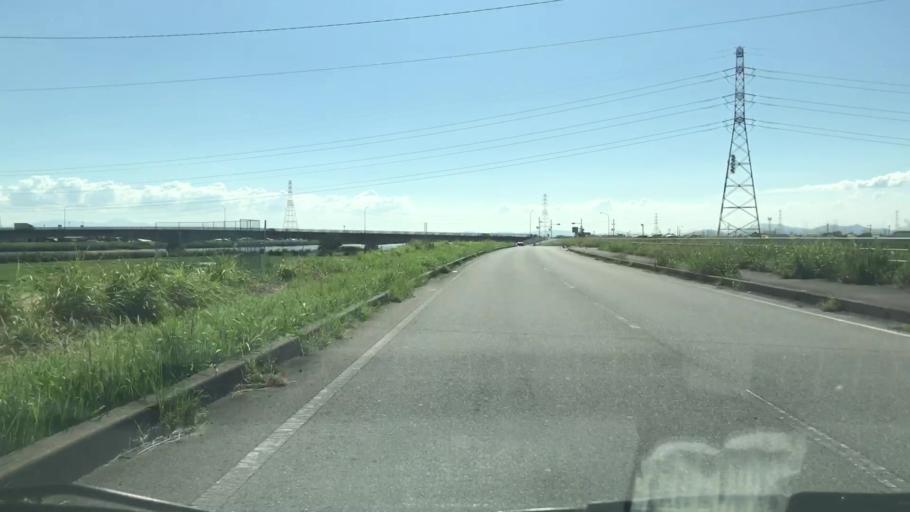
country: JP
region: Saga Prefecture
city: Kanzakimachi-kanzaki
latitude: 33.2520
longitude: 130.4089
